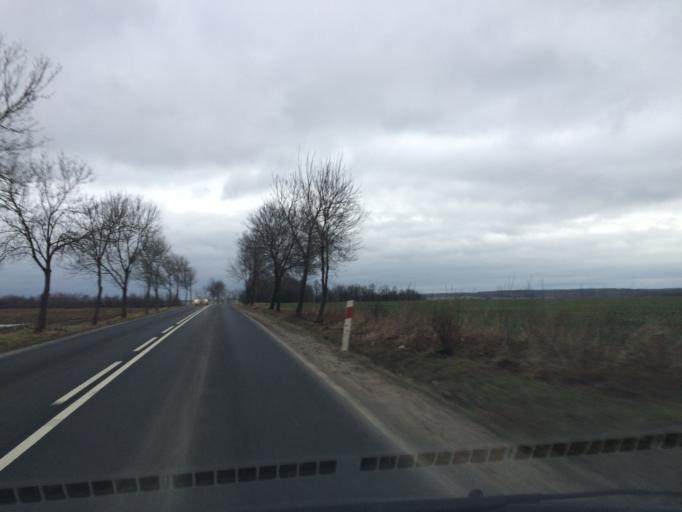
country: PL
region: Lower Silesian Voivodeship
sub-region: Powiat lubanski
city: Pisarzowice
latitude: 51.1577
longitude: 15.2671
